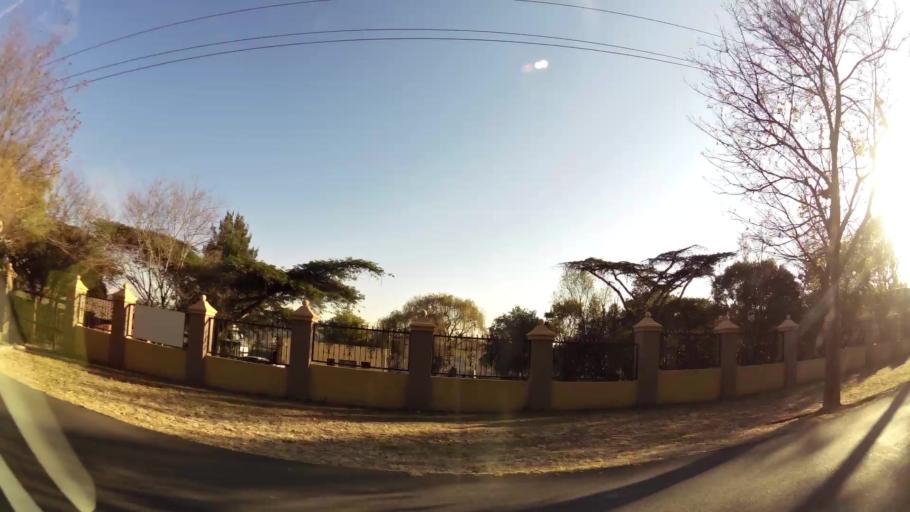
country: ZA
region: Gauteng
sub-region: City of Johannesburg Metropolitan Municipality
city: Midrand
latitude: -26.0224
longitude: 28.1426
